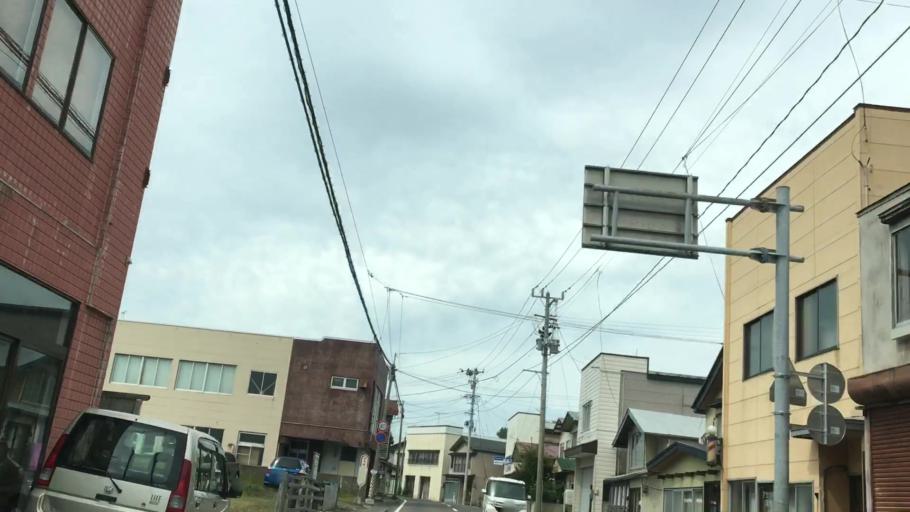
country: JP
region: Aomori
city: Shimokizukuri
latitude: 40.7780
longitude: 140.2175
